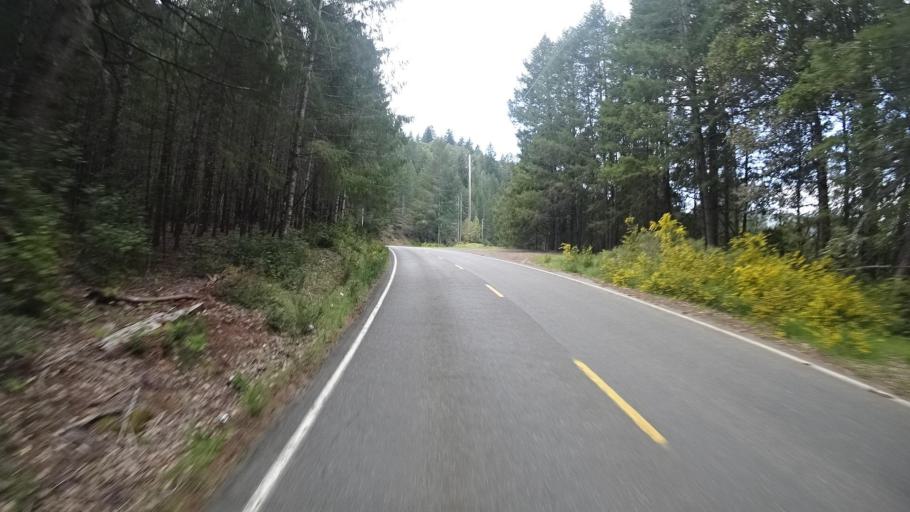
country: US
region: California
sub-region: Humboldt County
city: Redway
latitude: 40.0547
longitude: -123.9795
